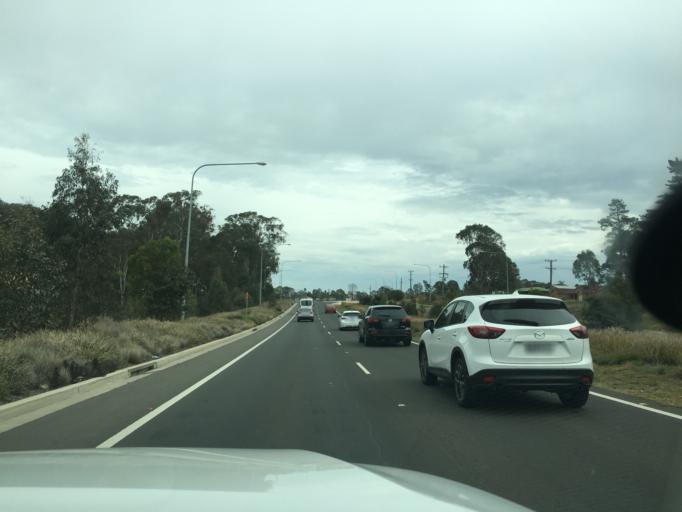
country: AU
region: New South Wales
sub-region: Campbelltown Municipality
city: Denham Court
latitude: -33.9805
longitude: 150.8024
